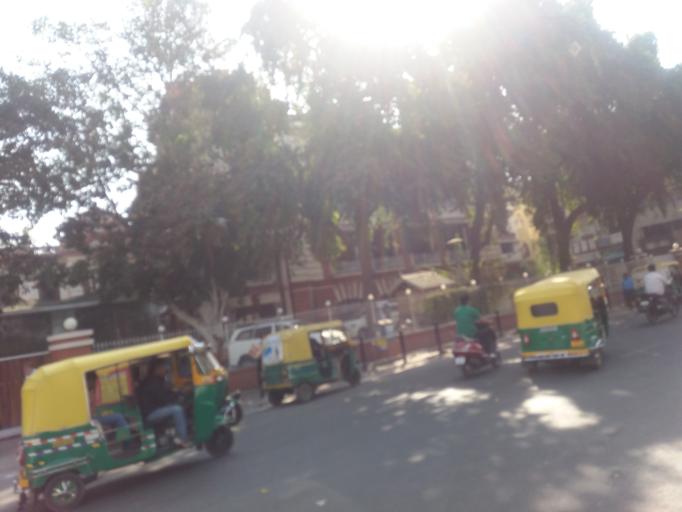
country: IN
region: Gujarat
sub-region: Ahmadabad
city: Ahmedabad
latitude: 23.0272
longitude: 72.5813
